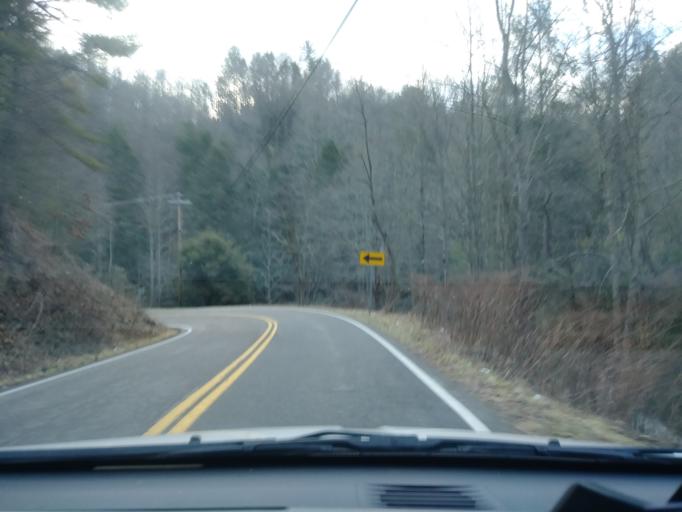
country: US
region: Tennessee
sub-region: Carter County
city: Elizabethton
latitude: 36.2142
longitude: -82.2127
